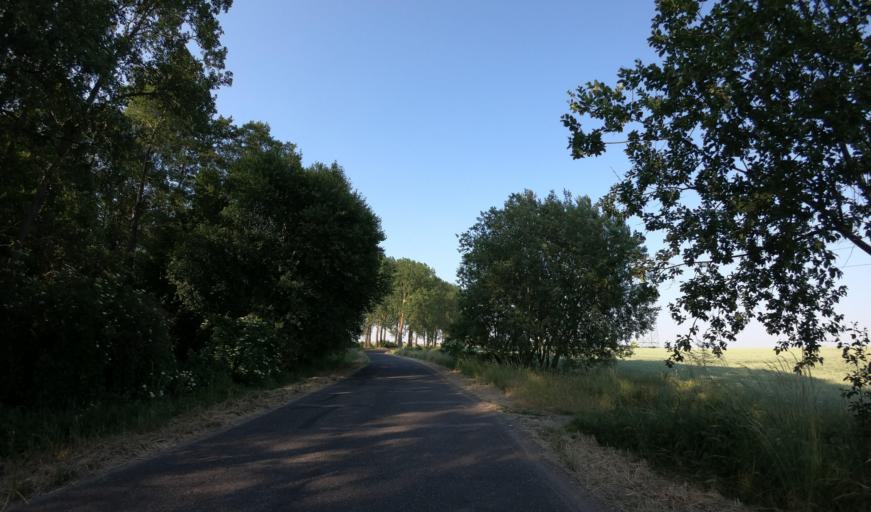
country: PL
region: West Pomeranian Voivodeship
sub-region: Powiat lobeski
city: Radowo Male
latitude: 53.6571
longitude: 15.4209
